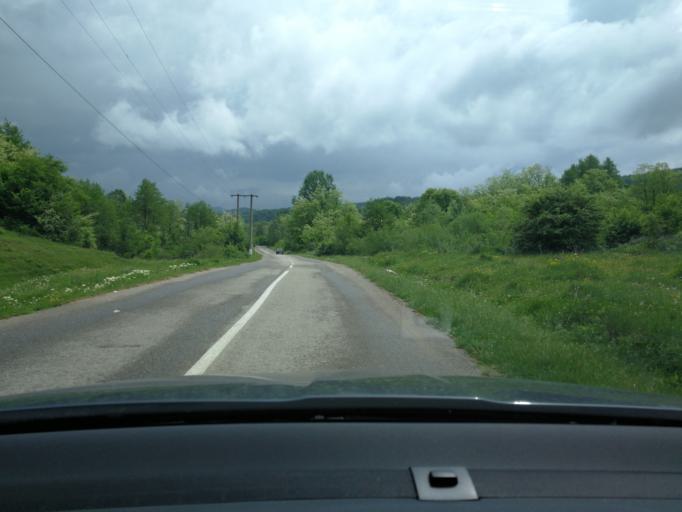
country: RO
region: Prahova
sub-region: Comuna Brebu
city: Pietriceaua
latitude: 45.2064
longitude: 25.8213
